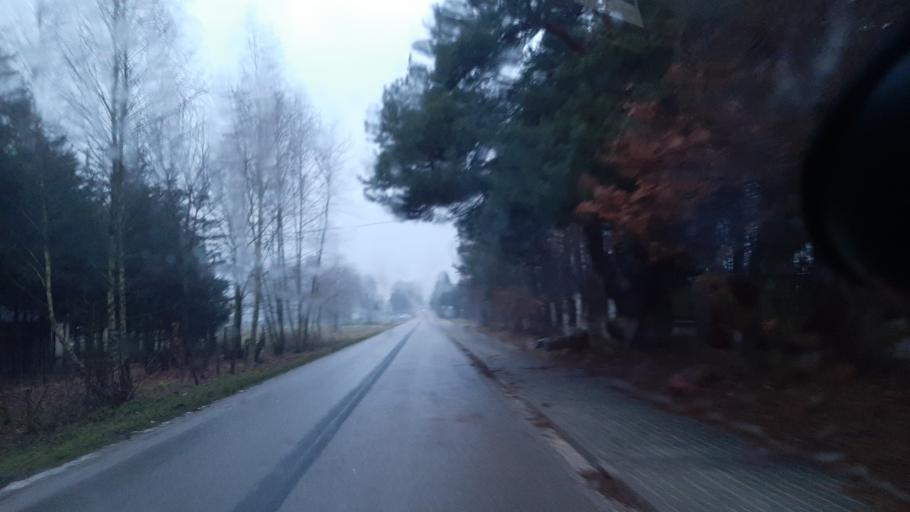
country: PL
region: Lublin Voivodeship
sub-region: Powiat lubartowski
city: Firlej
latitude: 51.5585
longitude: 22.5255
